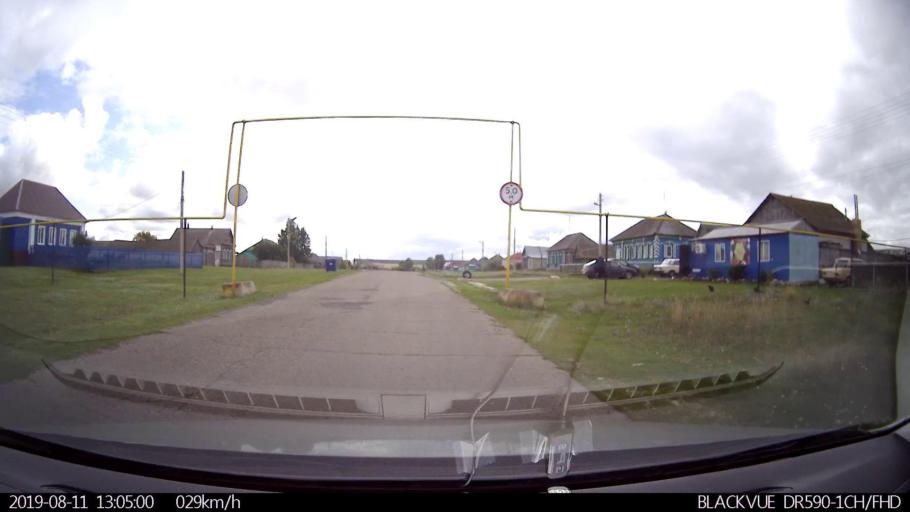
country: RU
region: Ulyanovsk
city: Ignatovka
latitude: 53.8727
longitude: 47.6485
